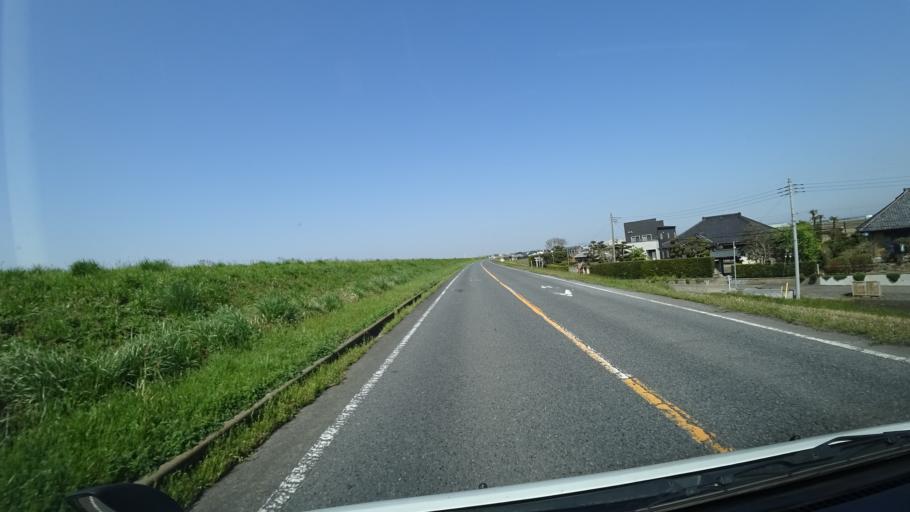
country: JP
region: Chiba
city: Katori-shi
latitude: 35.9131
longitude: 140.4836
